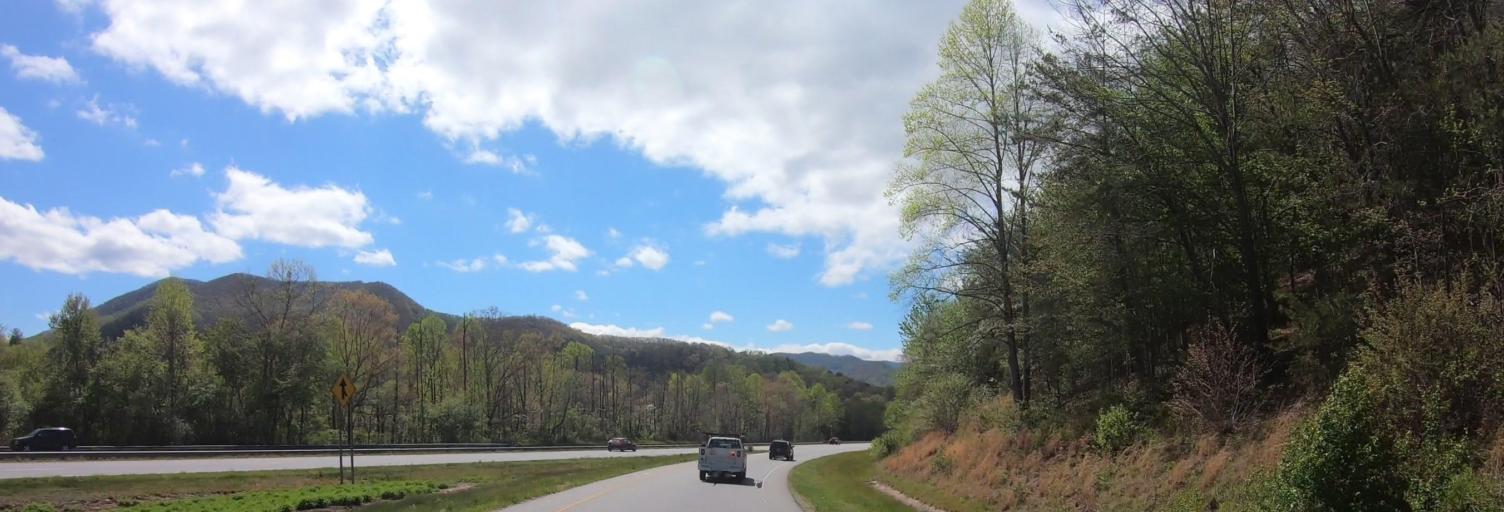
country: US
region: North Carolina
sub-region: Jackson County
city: Sylva
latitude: 35.3800
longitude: -83.2586
